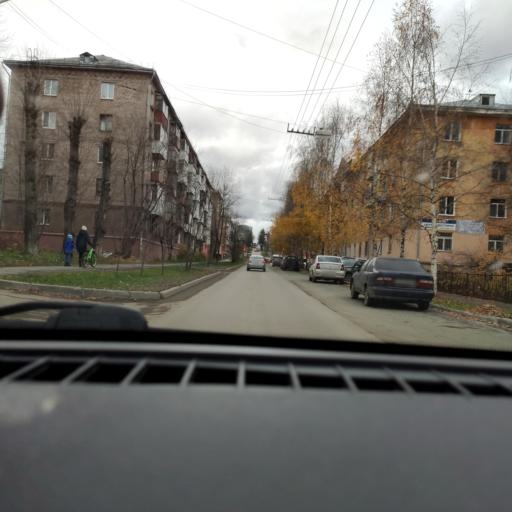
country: RU
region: Perm
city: Kondratovo
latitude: 57.9759
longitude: 56.1720
